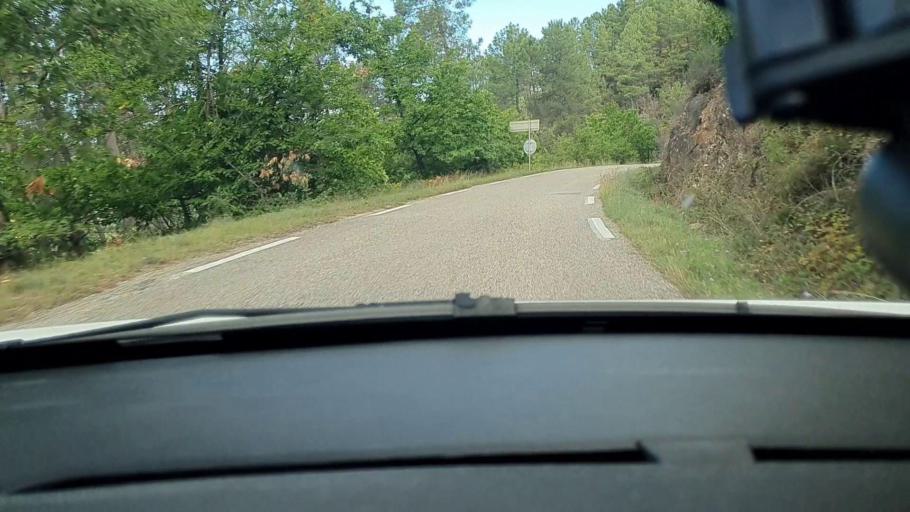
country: FR
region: Languedoc-Roussillon
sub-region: Departement du Gard
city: Besseges
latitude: 44.3239
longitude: 4.0721
